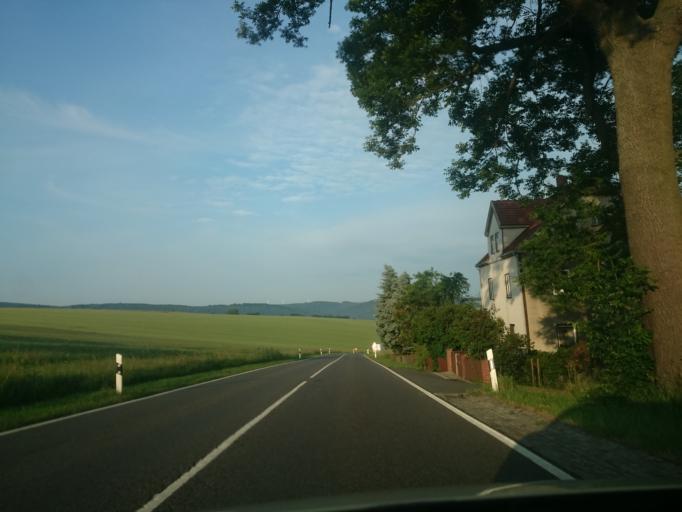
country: DE
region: Saxony
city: Pockau
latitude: 50.7115
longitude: 13.2493
